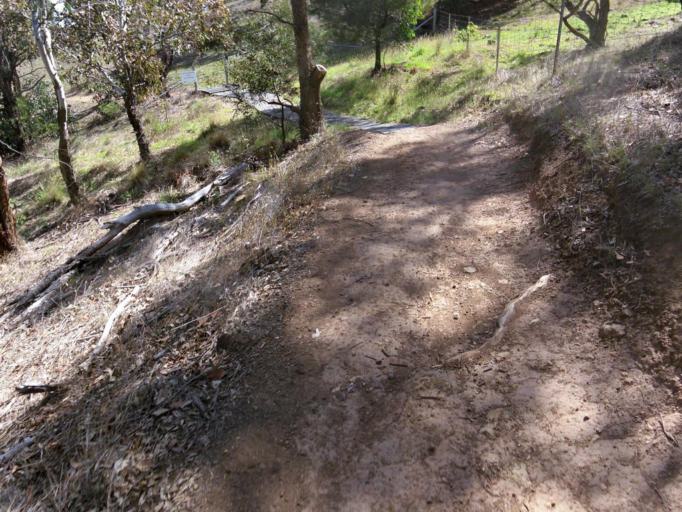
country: AU
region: Australian Capital Territory
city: Belconnen
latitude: -35.1531
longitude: 149.0858
